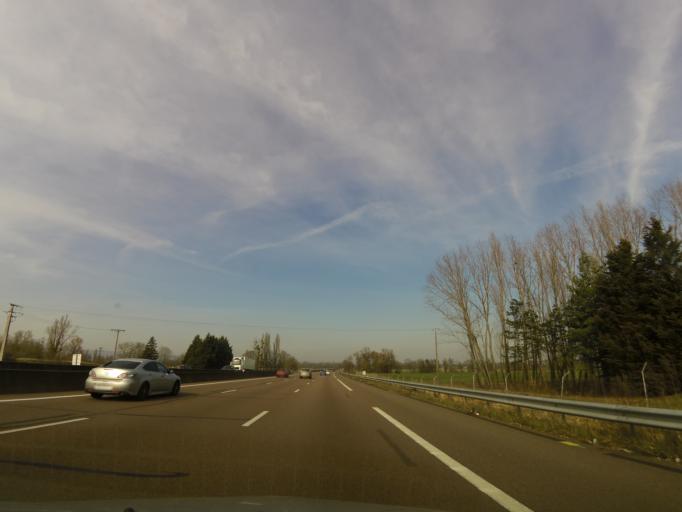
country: FR
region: Bourgogne
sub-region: Departement de Saone-et-Loire
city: Demigny
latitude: 46.9233
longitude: 4.8193
